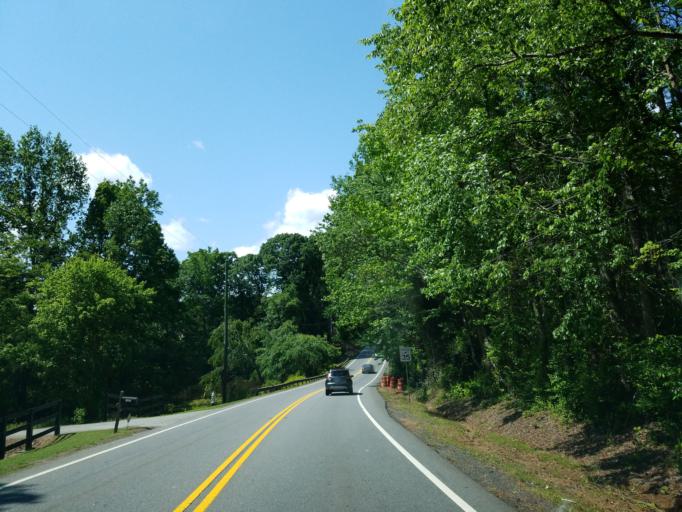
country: US
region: Georgia
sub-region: Fulton County
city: Roswell
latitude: 34.0716
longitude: -84.3520
